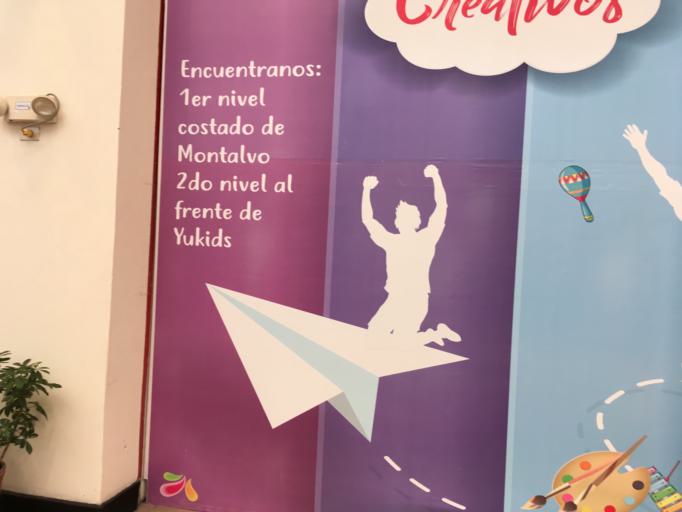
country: PE
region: Arequipa
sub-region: Provincia de Arequipa
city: Arequipa
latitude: -16.4108
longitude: -71.5208
